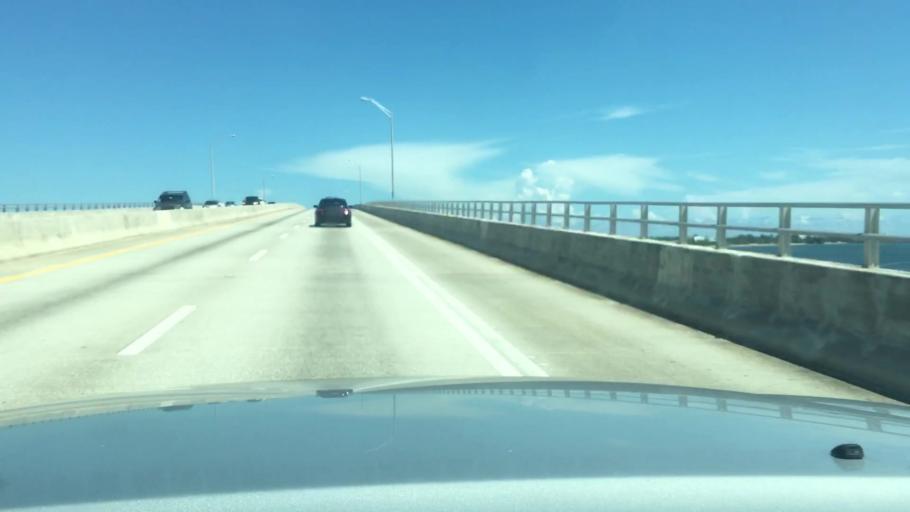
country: US
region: Florida
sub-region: Miami-Dade County
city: Miami
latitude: 25.7463
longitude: -80.1875
